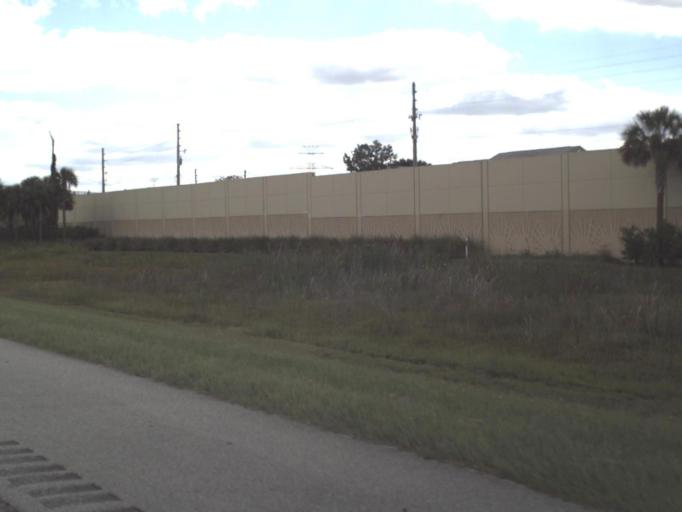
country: US
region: Florida
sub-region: Orange County
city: Tangelo Park
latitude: 28.4903
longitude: -81.4601
